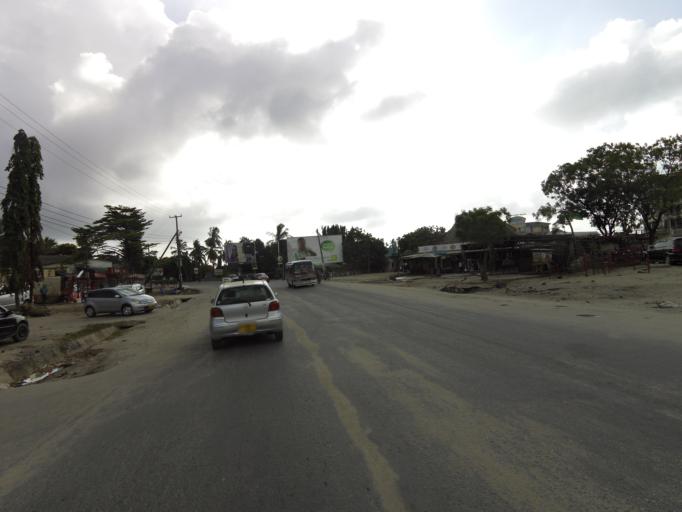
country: TZ
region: Dar es Salaam
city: Magomeni
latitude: -6.7743
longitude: 39.2338
